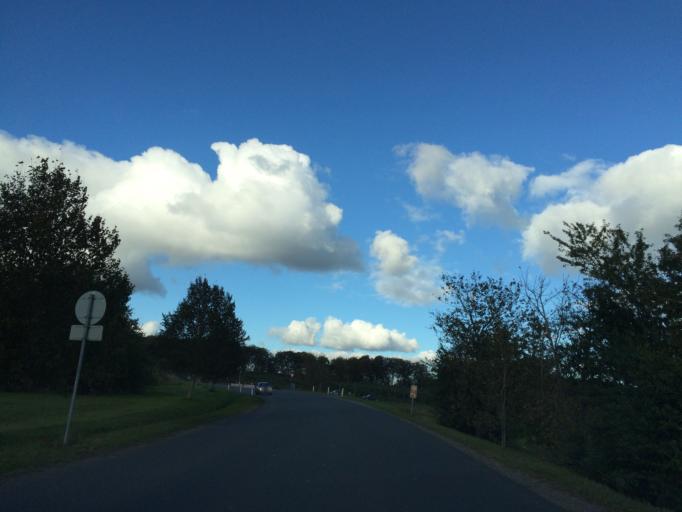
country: DK
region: Central Jutland
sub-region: Skanderborg Kommune
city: Ry
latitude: 56.0794
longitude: 9.7060
